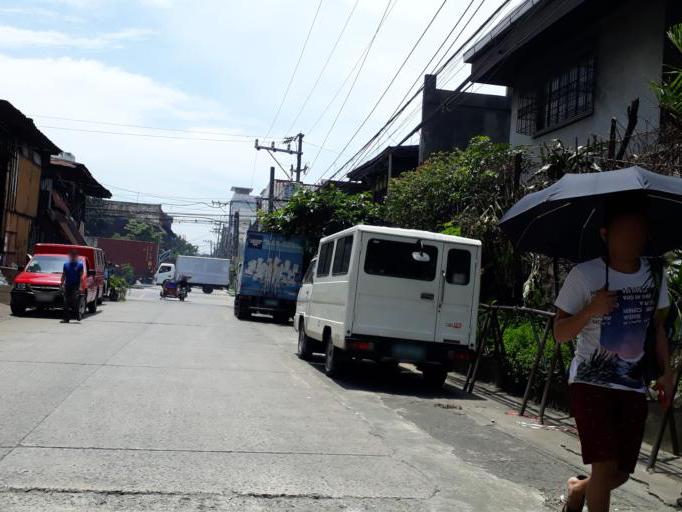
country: PH
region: Metro Manila
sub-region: Caloocan City
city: Niugan
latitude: 14.6453
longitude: 120.9806
